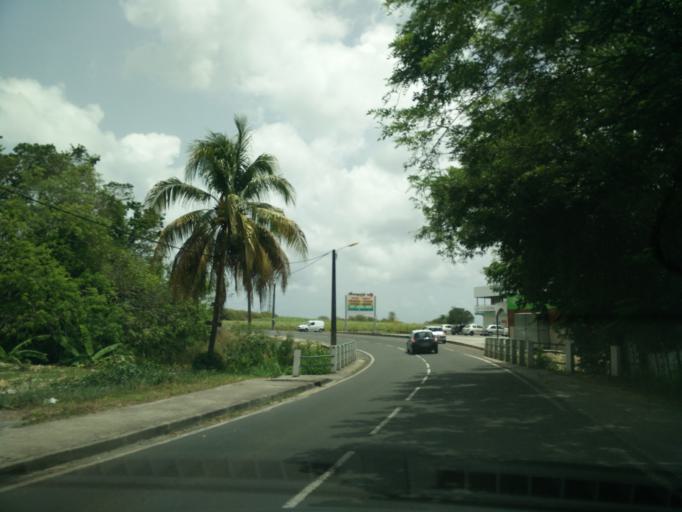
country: GP
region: Guadeloupe
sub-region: Guadeloupe
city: Port-Louis
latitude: 16.4142
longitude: -61.5190
